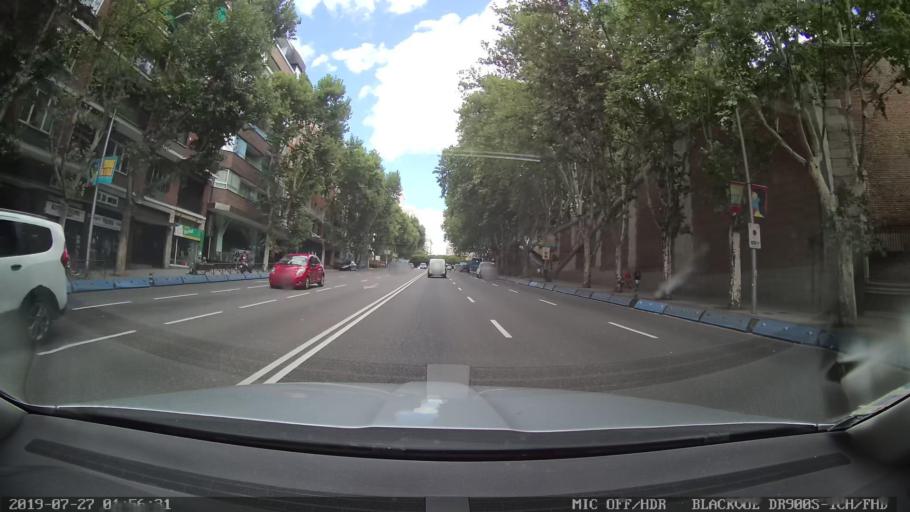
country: ES
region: Madrid
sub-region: Provincia de Madrid
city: City Center
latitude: 40.4195
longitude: -3.7166
